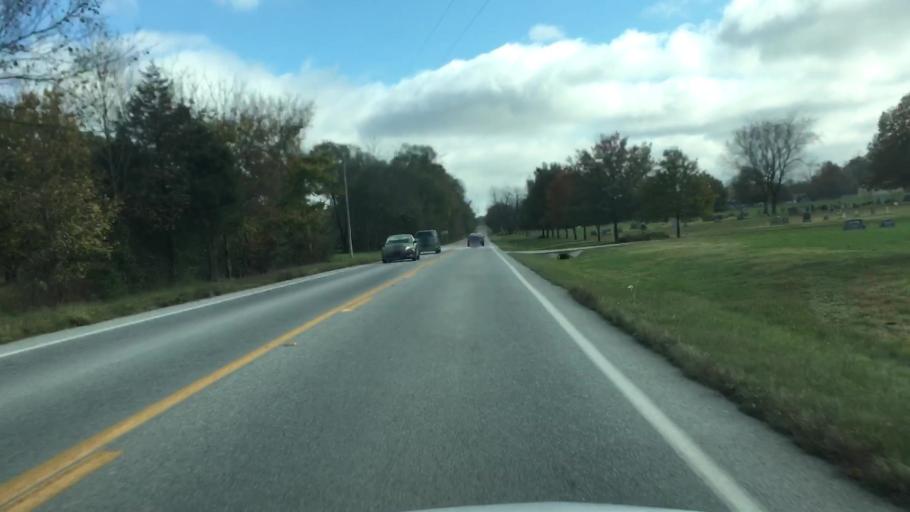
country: US
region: Arkansas
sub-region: Benton County
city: Gentry
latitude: 36.2609
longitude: -94.4181
